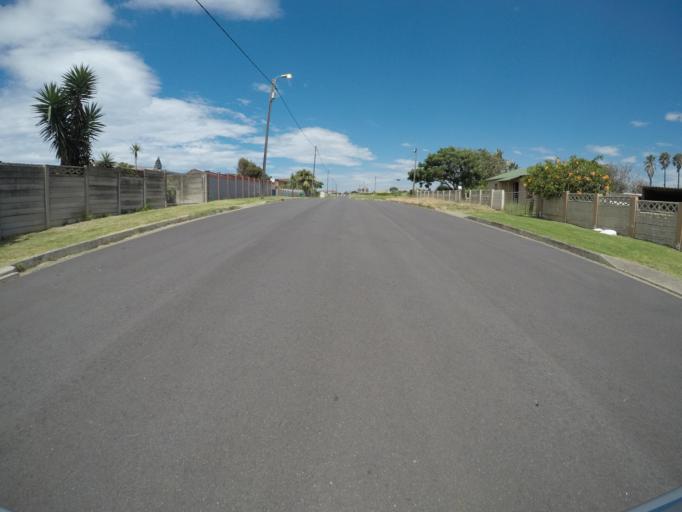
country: ZA
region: Eastern Cape
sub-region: Buffalo City Metropolitan Municipality
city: East London
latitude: -33.0383
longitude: 27.8864
